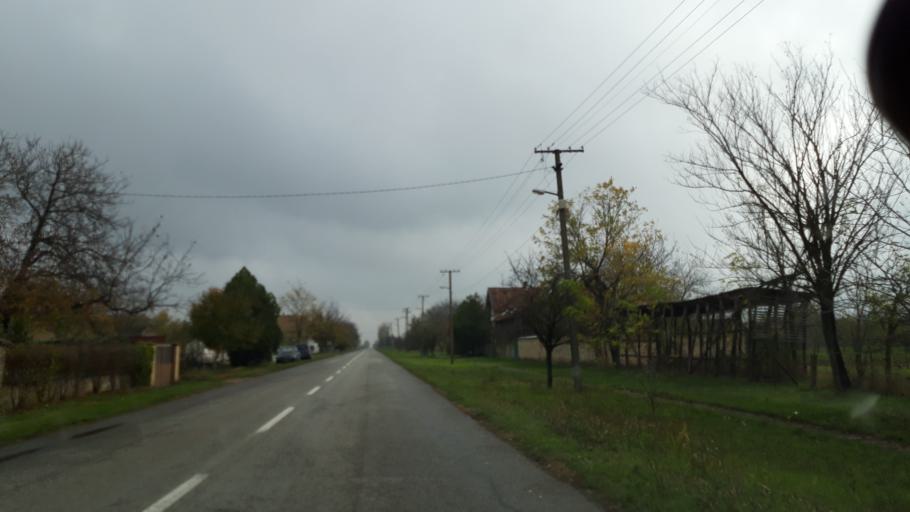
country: RS
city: Backo Gradiste
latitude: 45.5067
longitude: 19.9324
